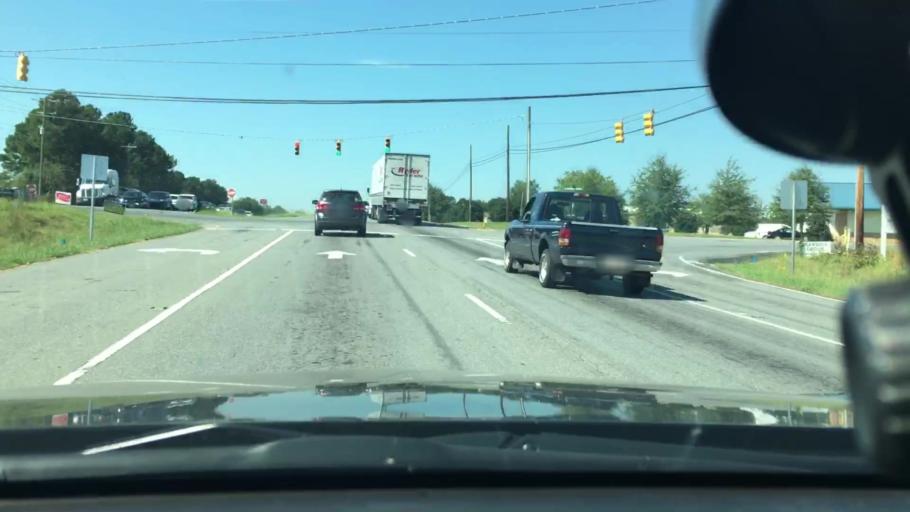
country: US
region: North Carolina
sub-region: Cleveland County
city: Shelby
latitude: 35.2936
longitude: -81.5977
